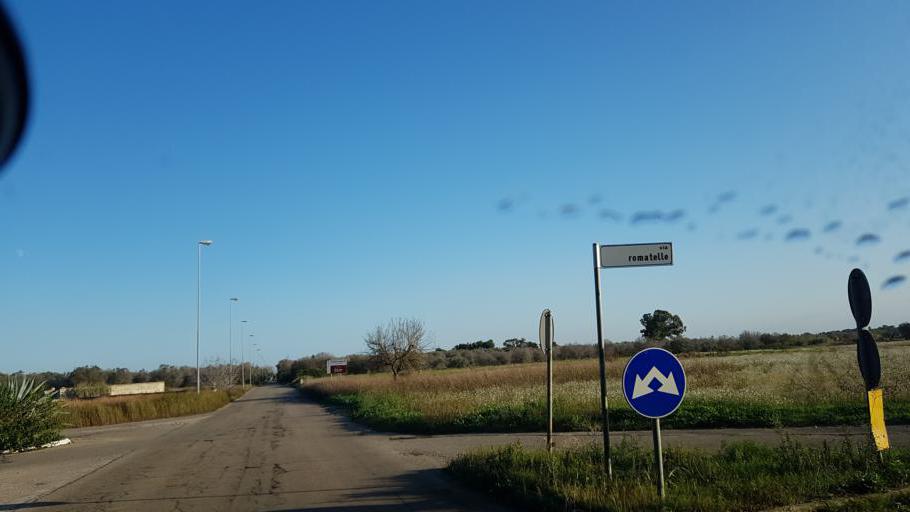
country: IT
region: Apulia
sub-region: Provincia di Brindisi
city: Torchiarolo
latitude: 40.5056
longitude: 18.1006
